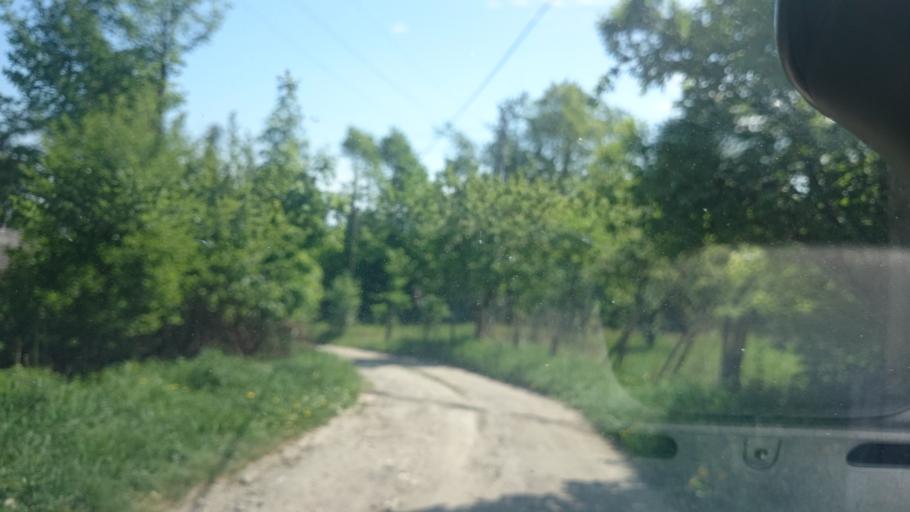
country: PL
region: Lower Silesian Voivodeship
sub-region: Powiat klodzki
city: Polanica-Zdroj
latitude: 50.3614
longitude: 16.5233
